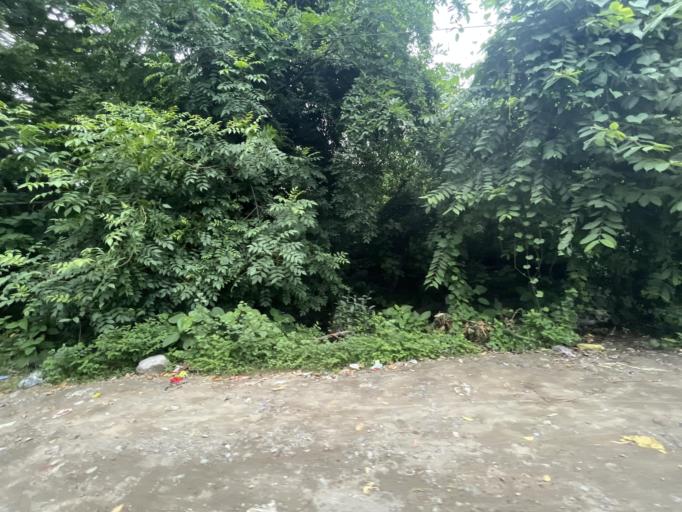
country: IN
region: Uttarakhand
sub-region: Naini Tal
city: Haldwani
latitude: 29.2023
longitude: 79.5161
